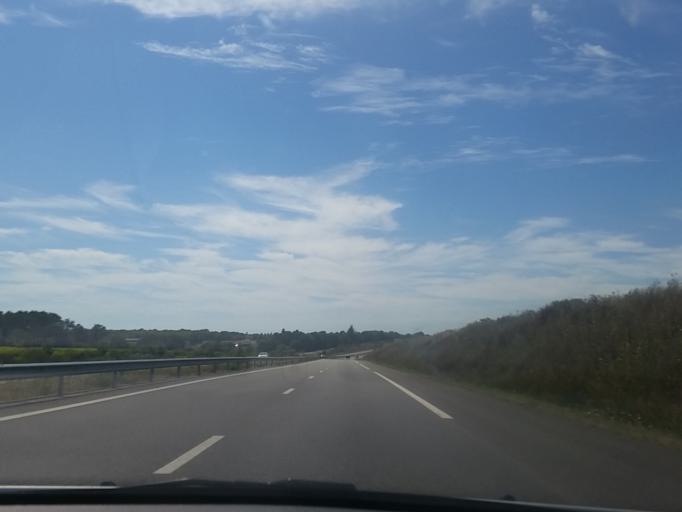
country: FR
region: Pays de la Loire
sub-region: Departement de la Loire-Atlantique
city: Le Pellerin
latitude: 47.1843
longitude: -1.7577
